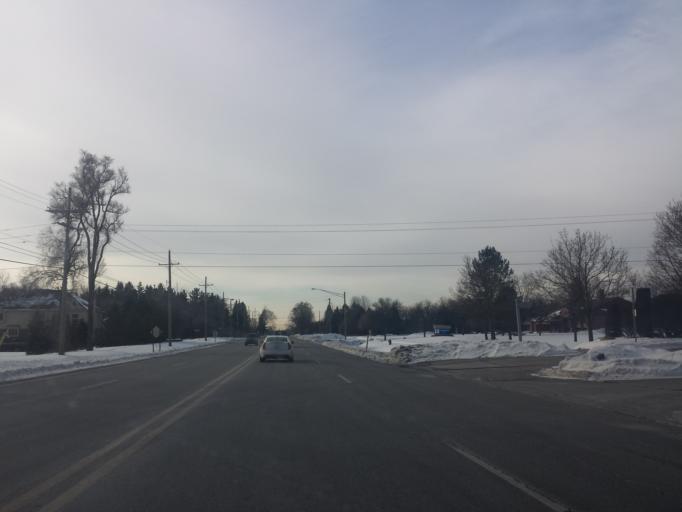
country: US
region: Michigan
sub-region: Oakland County
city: Franklin
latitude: 42.5048
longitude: -83.3394
